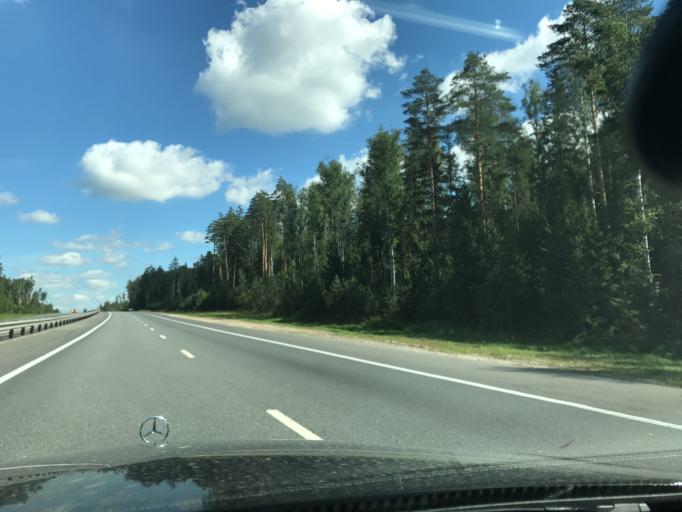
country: RU
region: Vladimir
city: Sudogda
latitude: 56.1496
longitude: 40.9161
